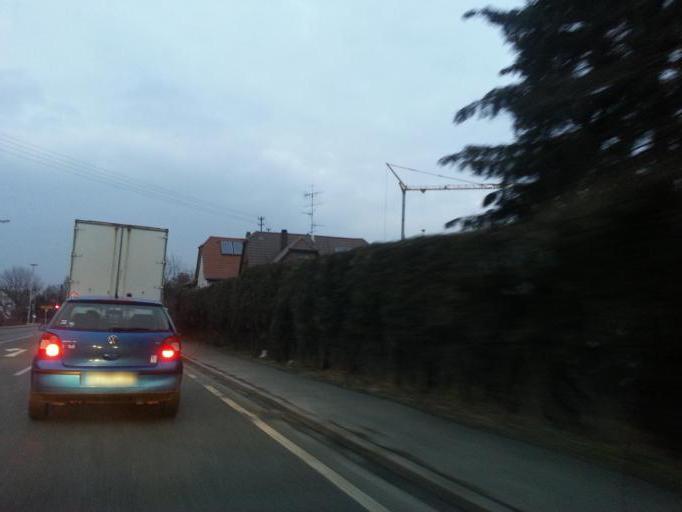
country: DE
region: Baden-Wuerttemberg
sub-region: Tuebingen Region
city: Bad Waldsee
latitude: 47.8942
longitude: 9.7190
